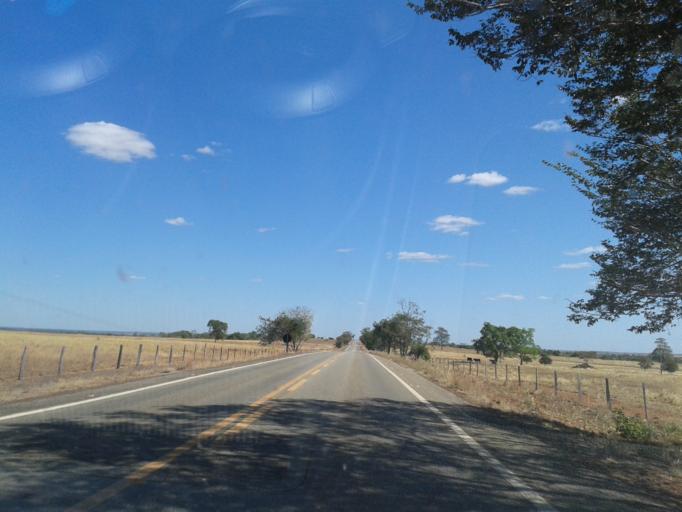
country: BR
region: Goias
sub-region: Sao Miguel Do Araguaia
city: Sao Miguel do Araguaia
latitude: -13.4055
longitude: -50.2620
